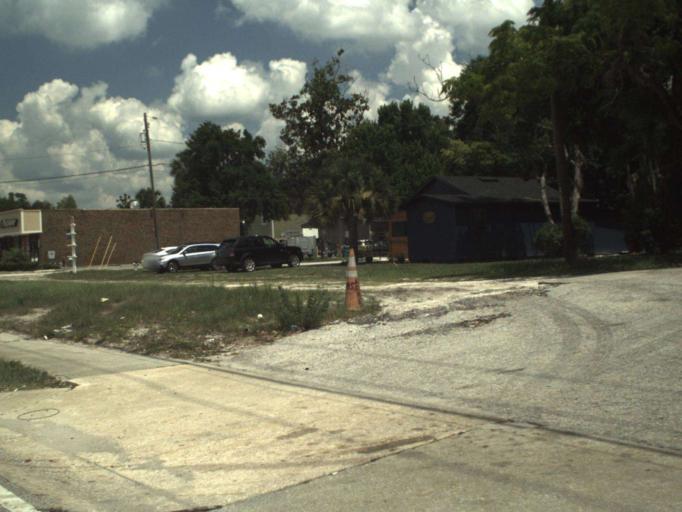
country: US
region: Florida
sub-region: Seminole County
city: Longwood
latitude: 28.6979
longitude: -81.3478
